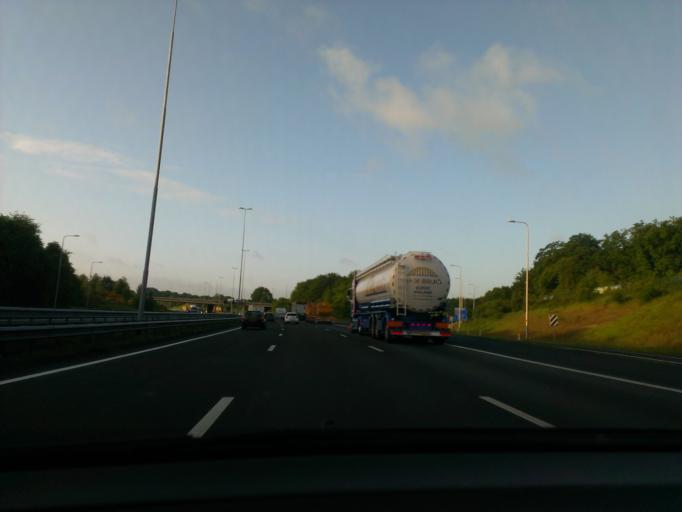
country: NL
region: Gelderland
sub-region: Gemeente Renkum
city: Heelsum
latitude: 51.9778
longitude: 5.7624
